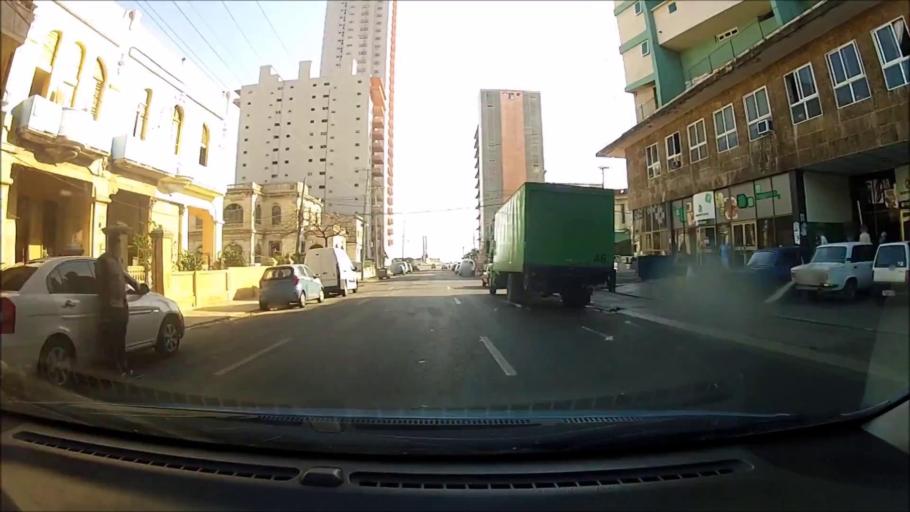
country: CU
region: La Habana
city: Havana
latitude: 23.1435
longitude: -82.3845
